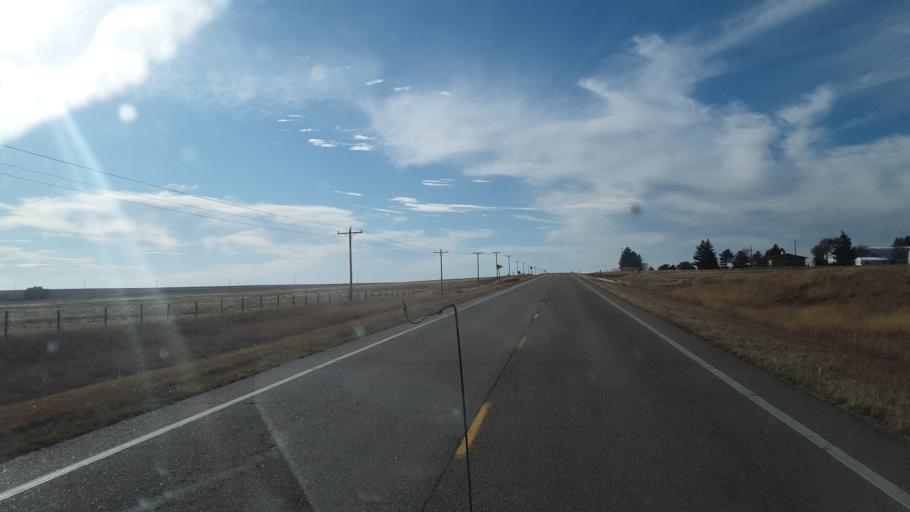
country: US
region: Kansas
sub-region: Finney County
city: Garden City
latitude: 38.0600
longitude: -100.6043
